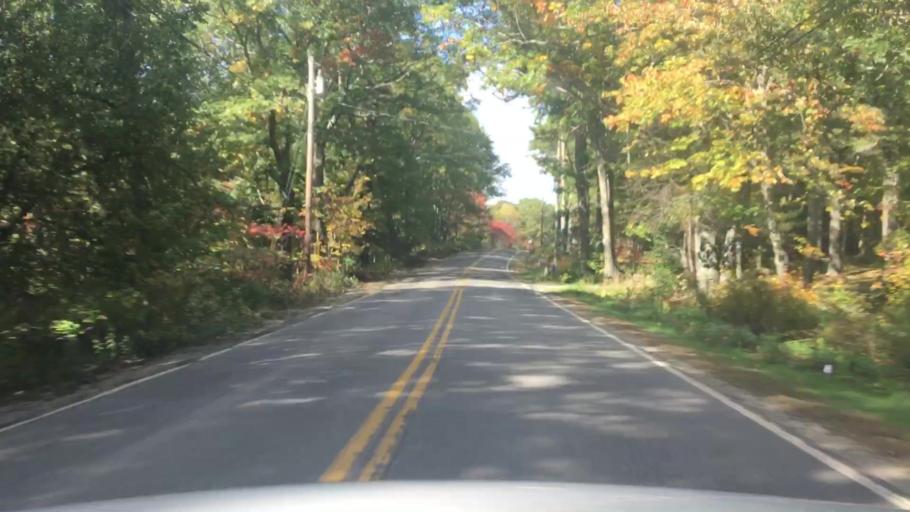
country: US
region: Maine
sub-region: Knox County
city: Warren
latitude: 44.1032
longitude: -69.2223
